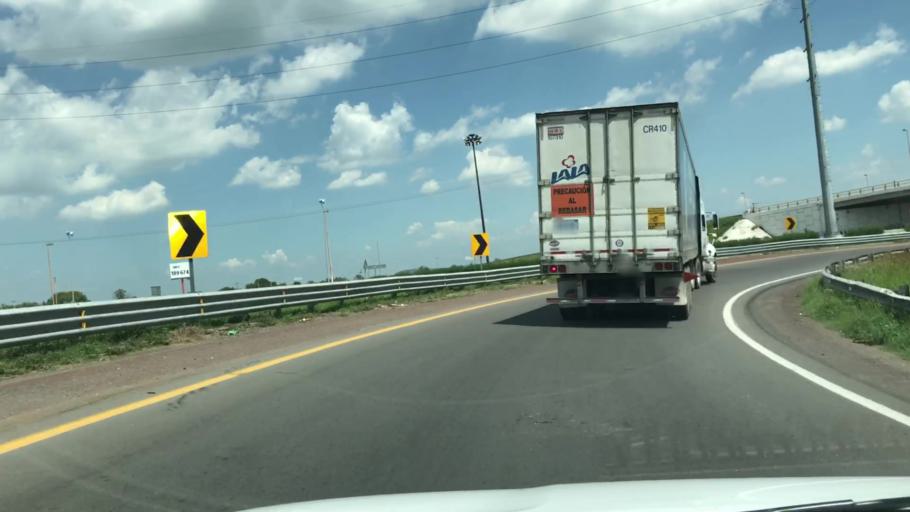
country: MX
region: Guanajuato
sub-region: Irapuato
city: Las Huertas Tercera Seccion
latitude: 20.6509
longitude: -101.3742
